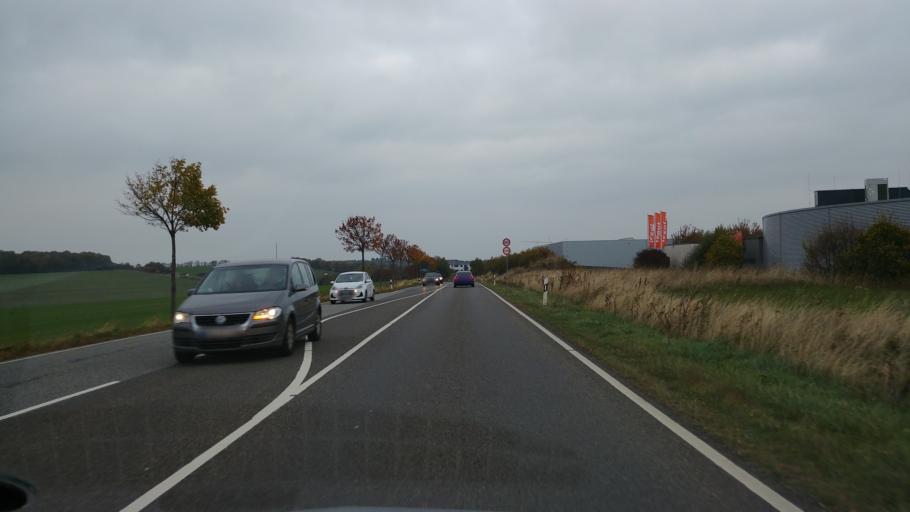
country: DE
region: Hesse
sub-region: Regierungsbezirk Darmstadt
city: Idstein
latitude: 50.2211
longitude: 8.1988
